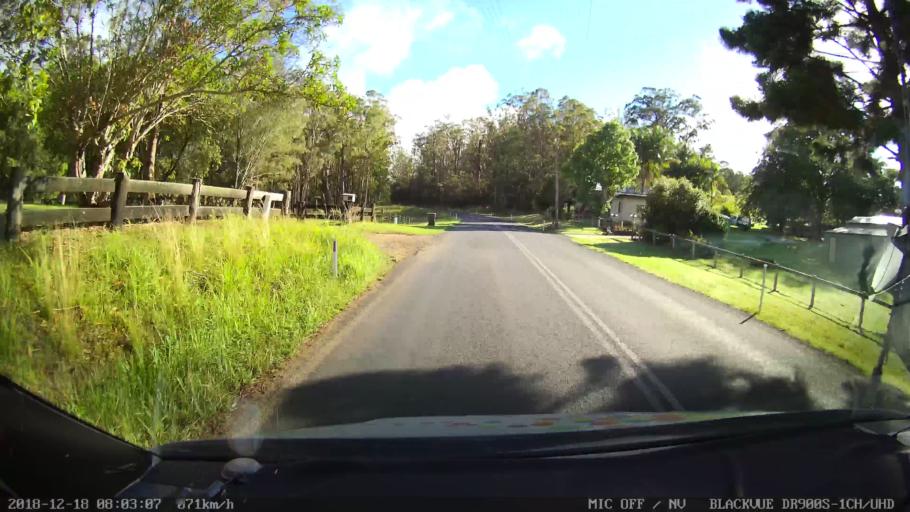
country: AU
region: New South Wales
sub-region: Kyogle
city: Kyogle
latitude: -28.3878
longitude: 152.6380
